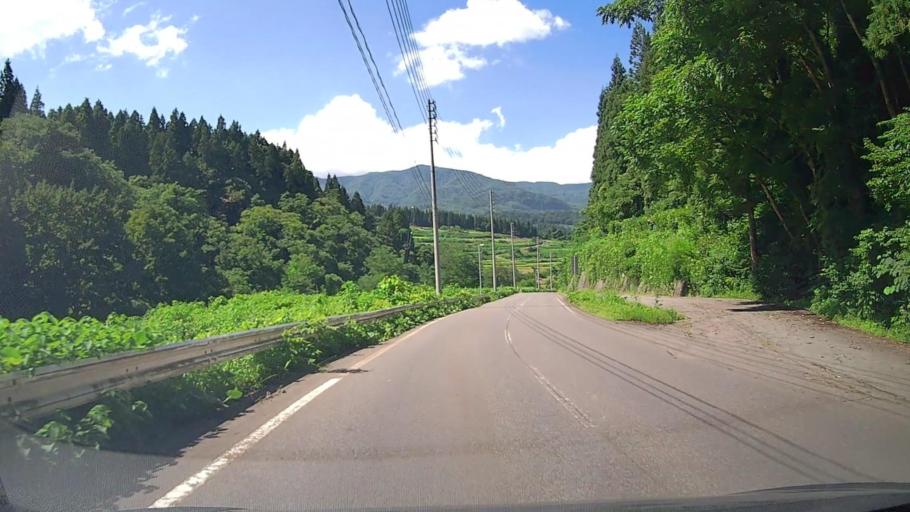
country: JP
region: Nagano
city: Iiyama
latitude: 36.9259
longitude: 138.4243
